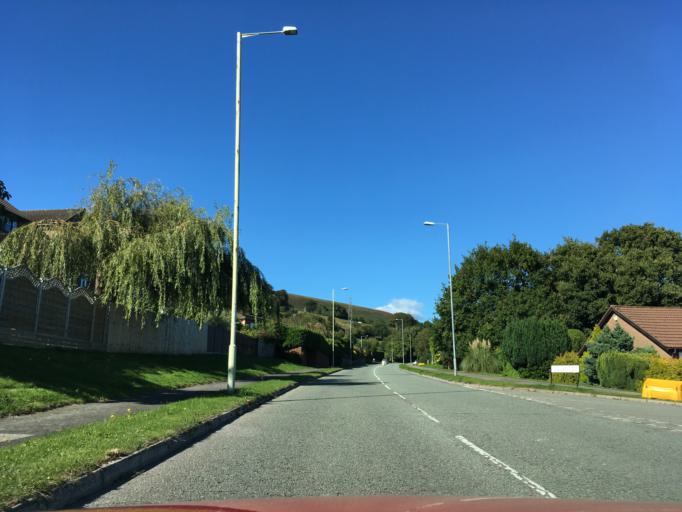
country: GB
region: Wales
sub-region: Torfaen County Borough
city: Cwmbran
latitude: 51.6455
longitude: -3.0601
